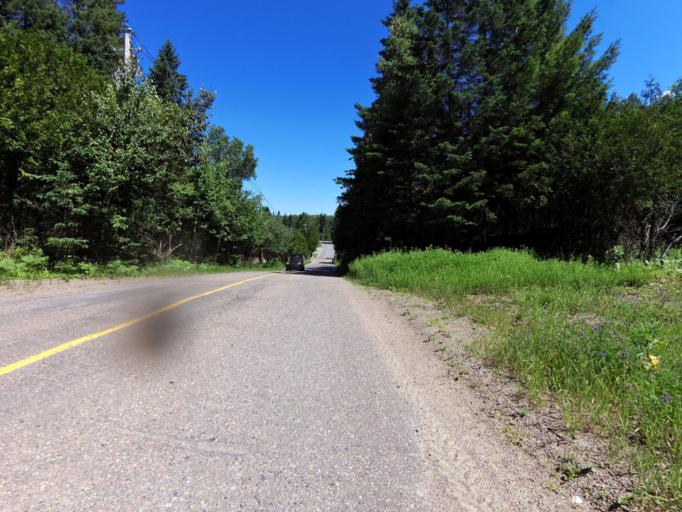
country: CA
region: Quebec
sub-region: Laurentides
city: Brownsburg-Chatham
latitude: 45.8431
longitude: -74.4710
